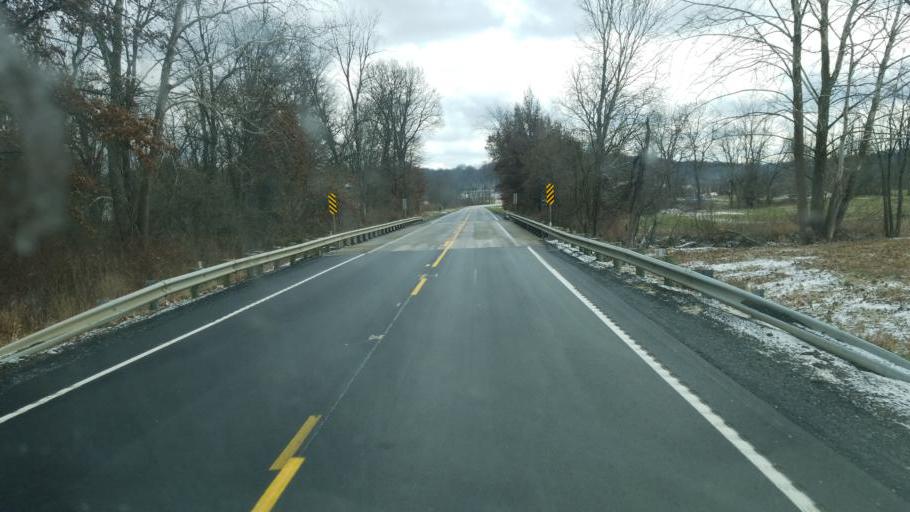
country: US
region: Ohio
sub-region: Muskingum County
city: Frazeysburg
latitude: 40.1366
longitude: -82.2033
